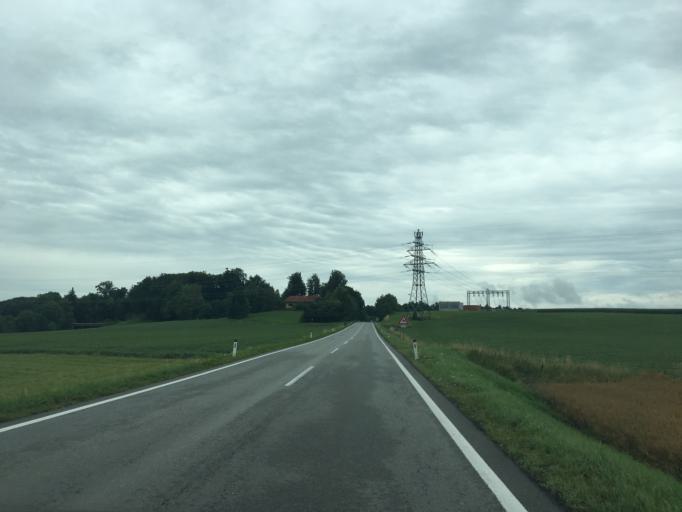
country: AT
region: Salzburg
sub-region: Politischer Bezirk Salzburg-Umgebung
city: Dorfbeuern
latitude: 48.0939
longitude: 12.9920
